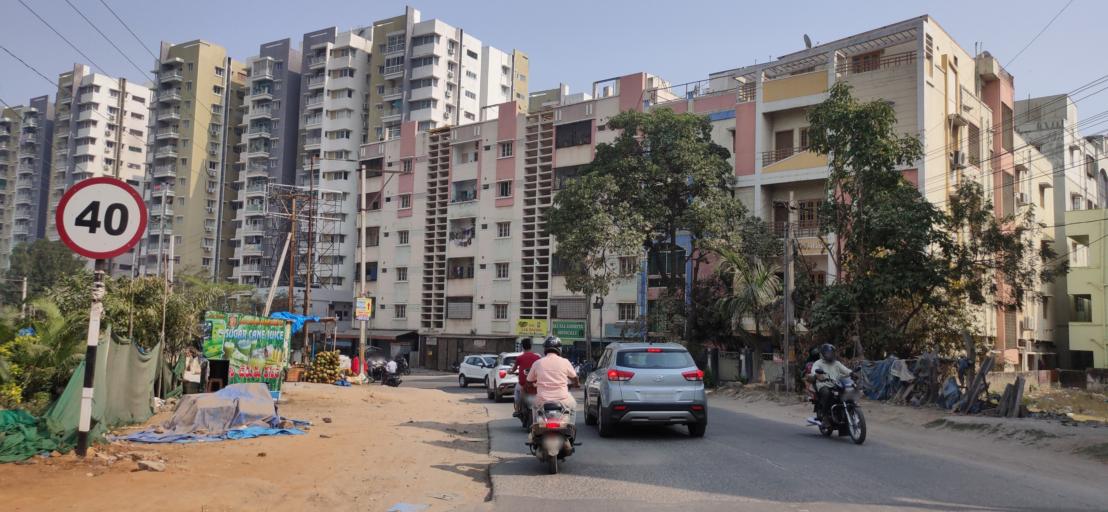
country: IN
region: Telangana
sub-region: Rangareddi
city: Kukatpalli
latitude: 17.5001
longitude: 78.4089
